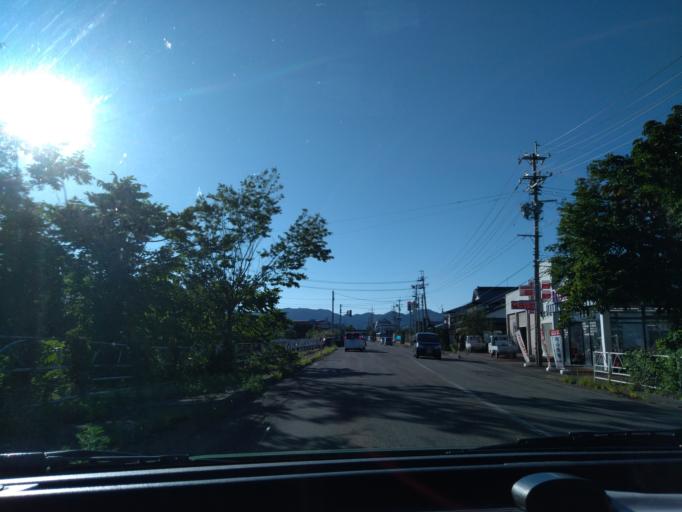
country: JP
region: Akita
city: Omagari
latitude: 39.4268
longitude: 140.4911
